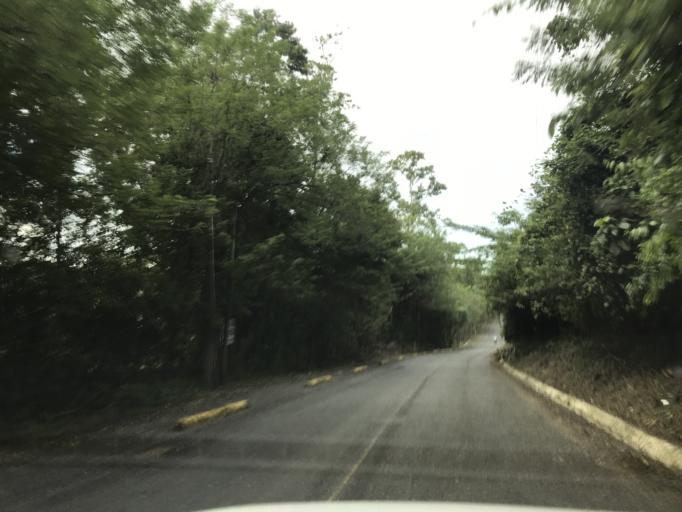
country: GT
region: Izabal
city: Morales
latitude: 15.6449
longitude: -89.0094
